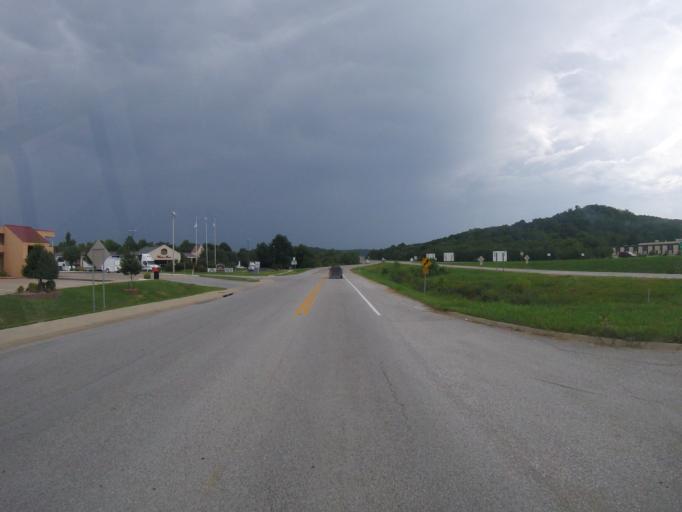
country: US
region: Arkansas
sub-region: Washington County
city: Fayetteville
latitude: 36.0529
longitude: -94.1930
